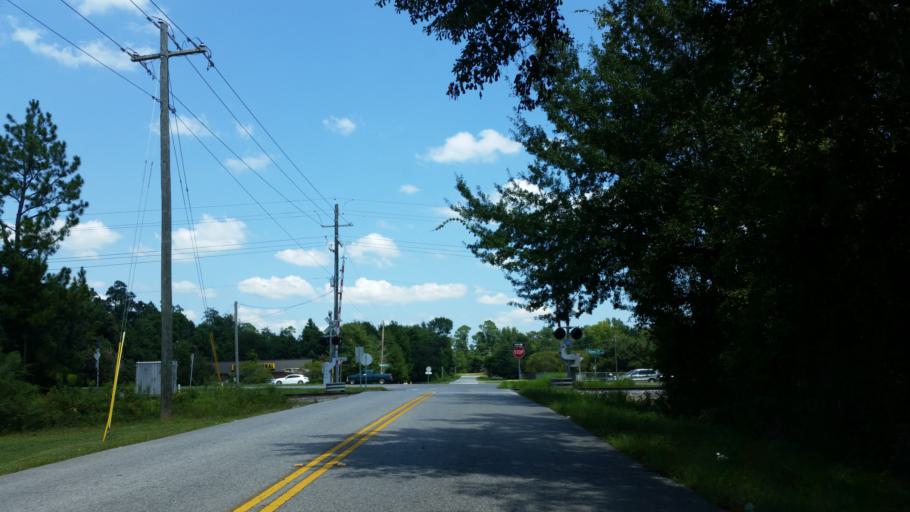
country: US
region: Florida
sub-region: Escambia County
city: Gonzalez
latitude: 30.5801
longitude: -87.2984
